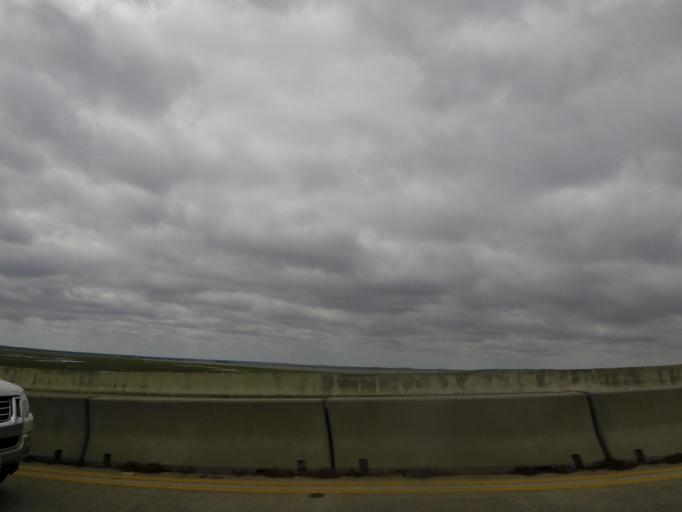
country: US
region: Georgia
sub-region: Glynn County
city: Saint Simon Mills
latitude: 31.1719
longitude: -81.4273
